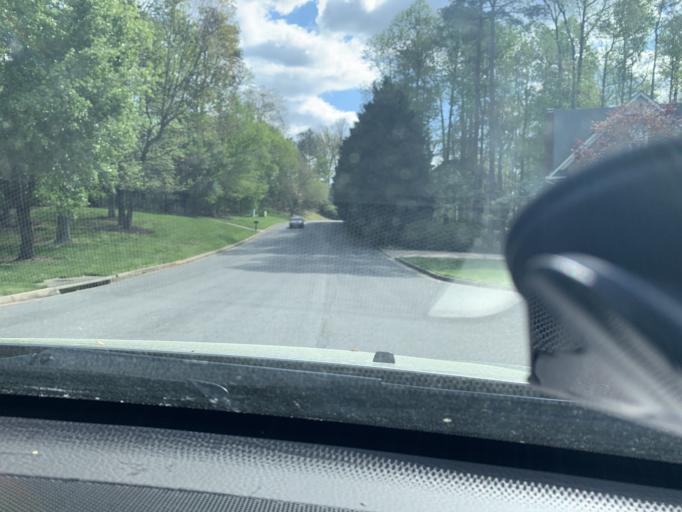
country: US
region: Virginia
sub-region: Henrico County
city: Tuckahoe
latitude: 37.5912
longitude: -77.6028
